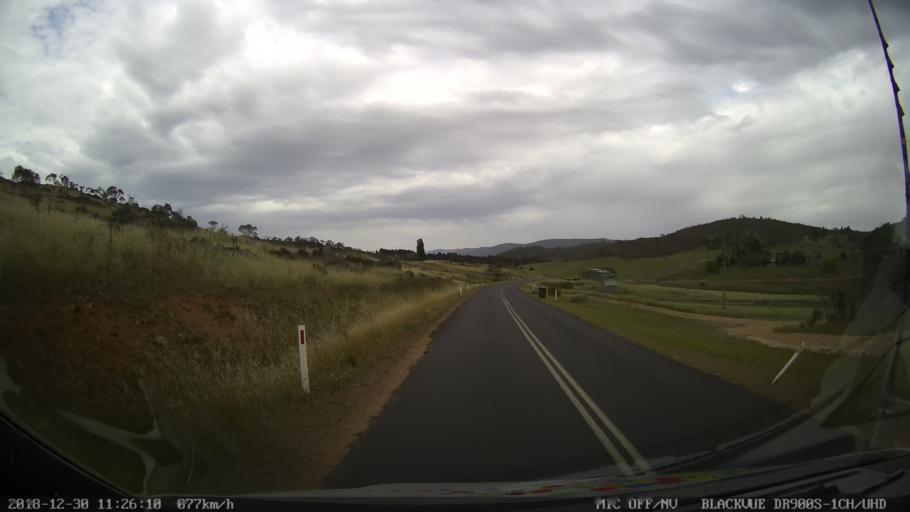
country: AU
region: New South Wales
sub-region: Snowy River
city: Jindabyne
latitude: -36.4689
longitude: 148.6376
